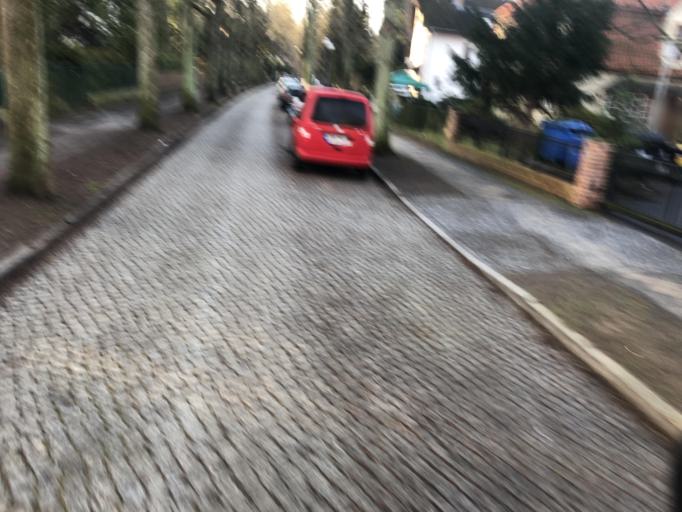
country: DE
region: Berlin
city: Frohnau
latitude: 52.6318
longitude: 13.2879
